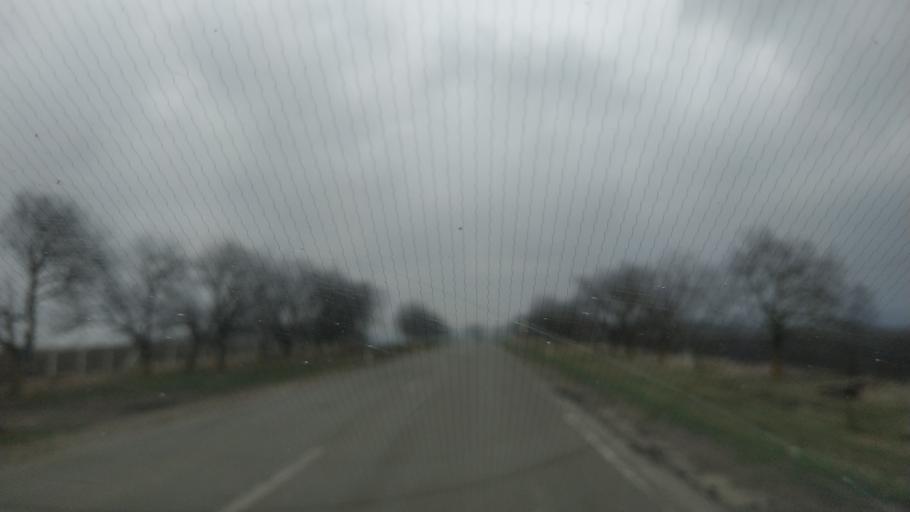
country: MD
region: Gagauzia
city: Comrat
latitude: 46.2631
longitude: 28.7447
